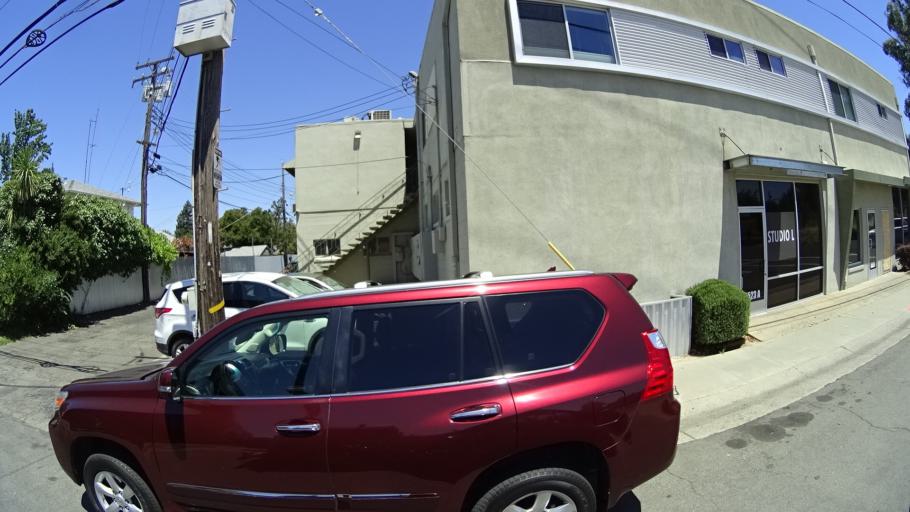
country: US
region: California
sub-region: Sacramento County
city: Sacramento
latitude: 38.5706
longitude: -121.4336
